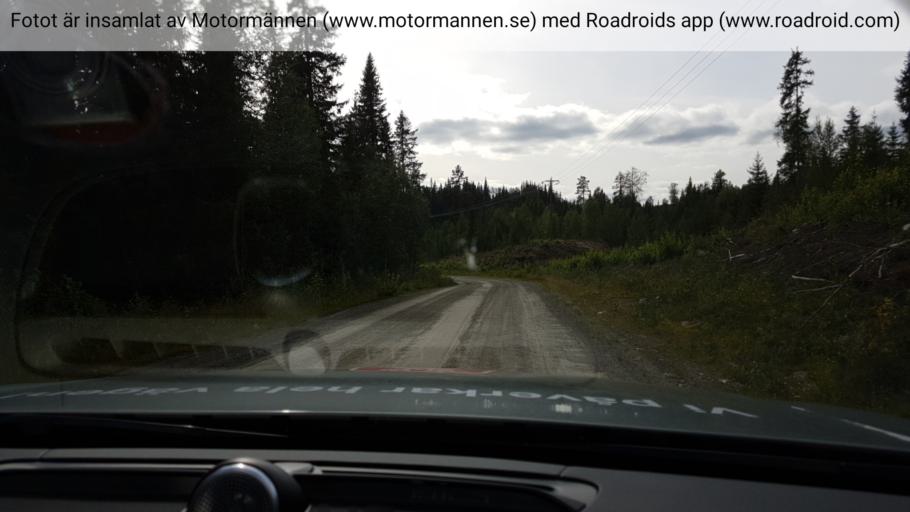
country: SE
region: Jaemtland
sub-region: Stroemsunds Kommun
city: Stroemsund
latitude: 64.5246
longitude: 15.2140
